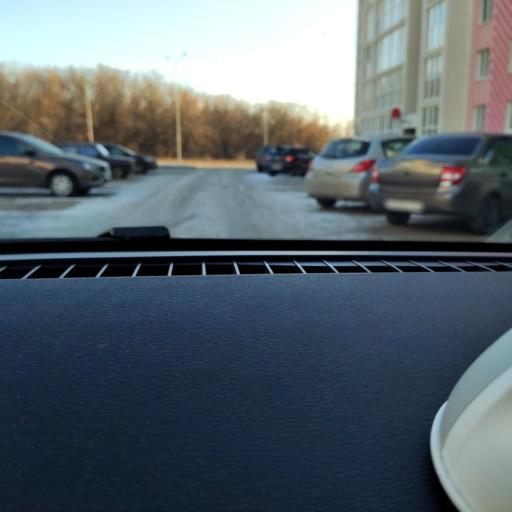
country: RU
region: Samara
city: Petra-Dubrava
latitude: 53.2986
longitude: 50.3325
